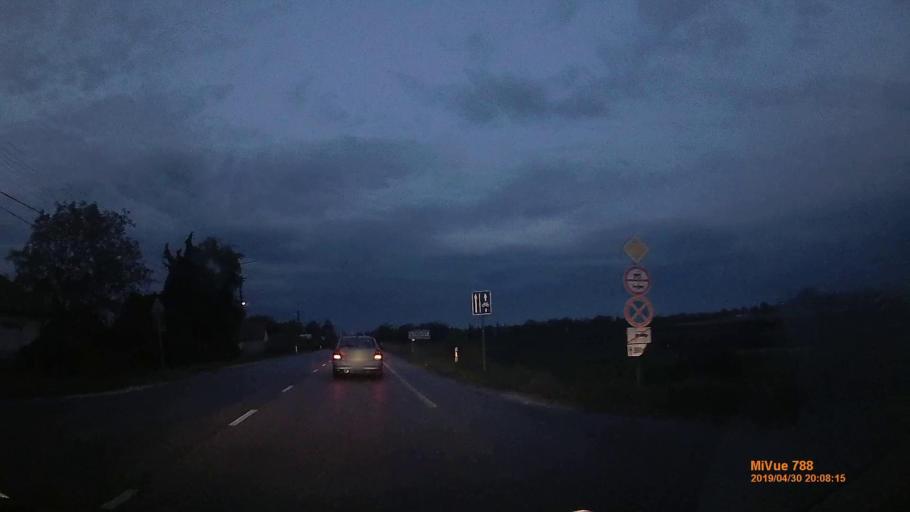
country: HU
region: Pest
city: Abony
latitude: 47.1843
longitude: 20.0358
